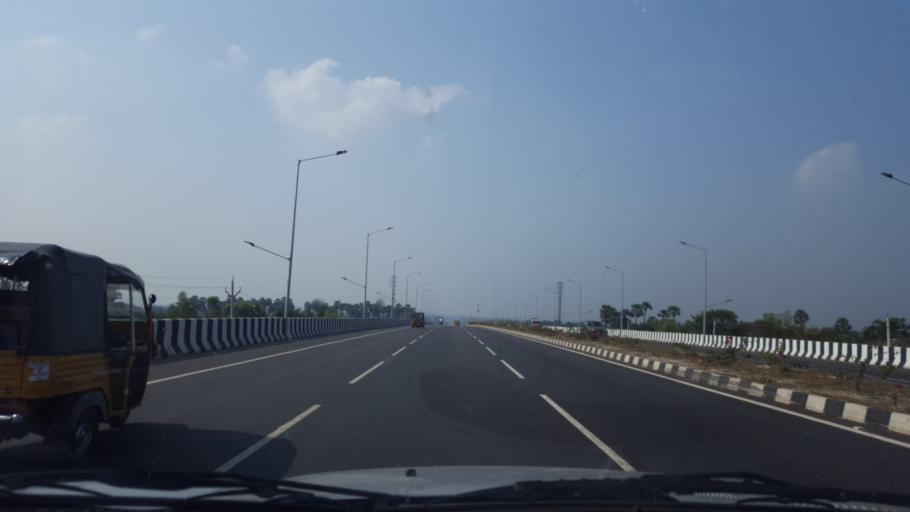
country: IN
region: Andhra Pradesh
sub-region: Vizianagaram District
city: Vizianagaram
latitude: 18.0514
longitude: 83.5162
